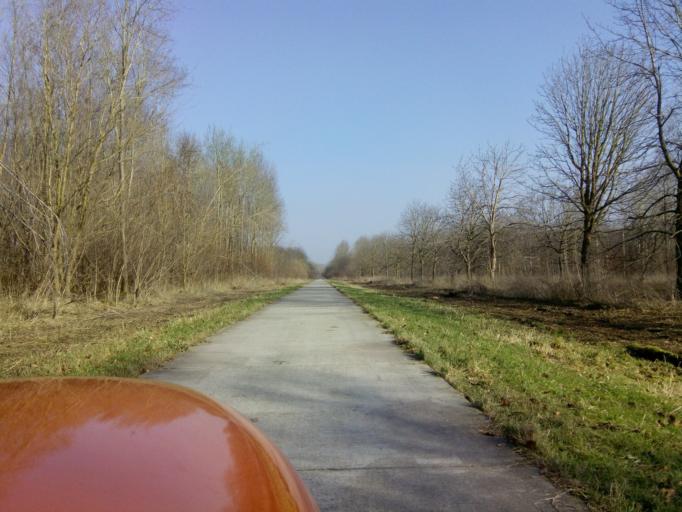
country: NL
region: Flevoland
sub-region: Gemeente Zeewolde
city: Zeewolde
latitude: 52.3393
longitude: 5.4635
